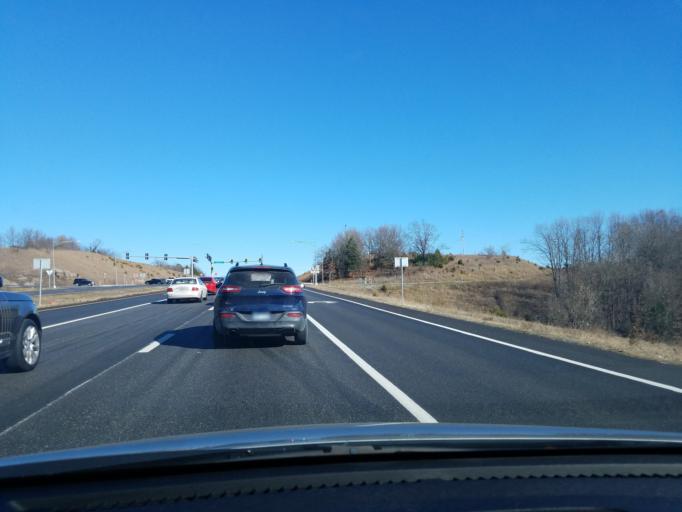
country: US
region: Missouri
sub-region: Taney County
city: Hollister
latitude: 36.5686
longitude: -93.2510
